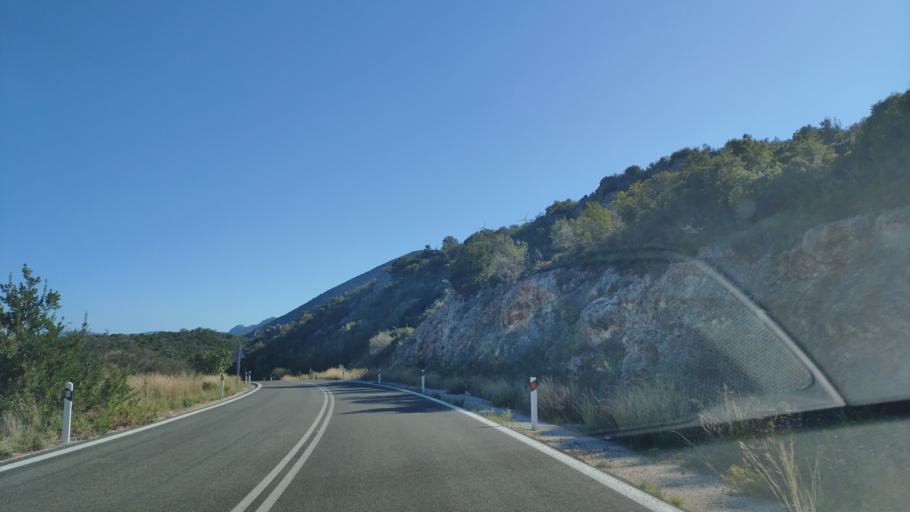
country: GR
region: Peloponnese
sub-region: Nomos Argolidos
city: Palaia Epidavros
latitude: 37.5640
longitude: 23.2540
